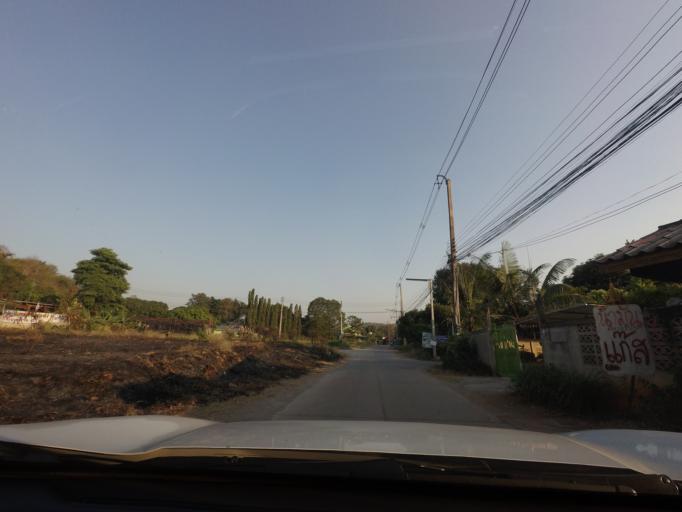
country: TH
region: Nakhon Ratchasima
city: Pak Chong
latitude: 14.6432
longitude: 101.3568
